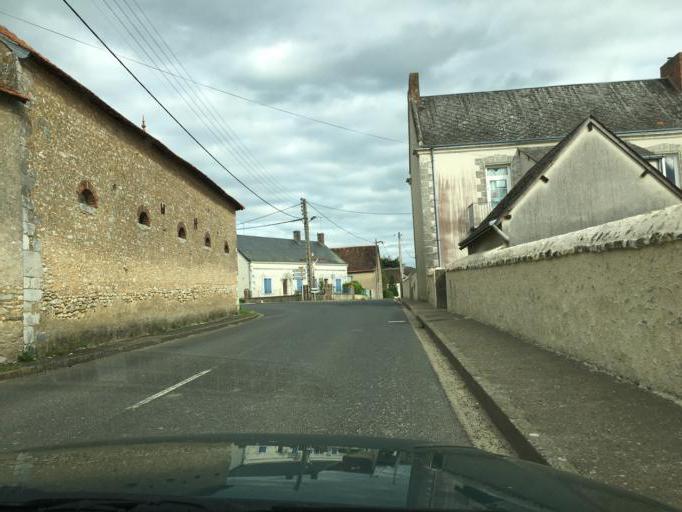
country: FR
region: Centre
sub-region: Departement du Loir-et-Cher
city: Saint-Ouen
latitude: 47.7838
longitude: 1.1441
